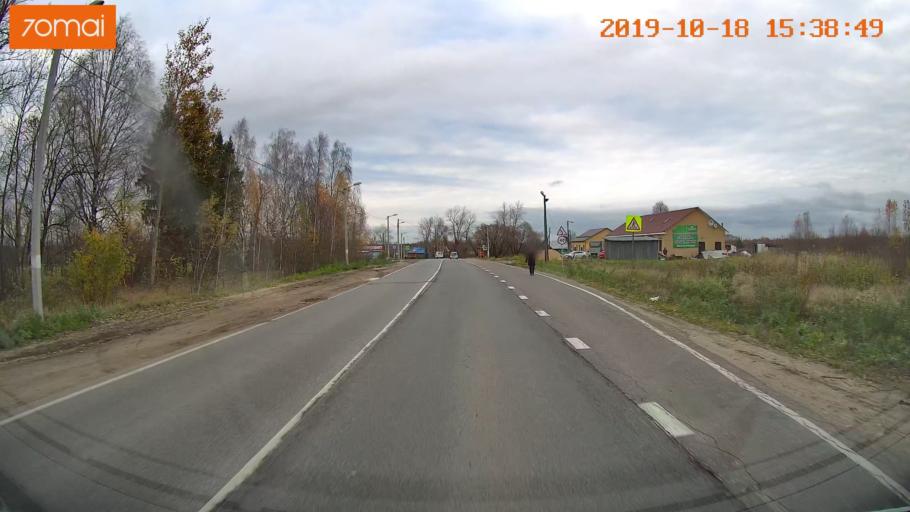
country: RU
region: Vladimir
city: Golovino
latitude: 55.9159
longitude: 40.6075
